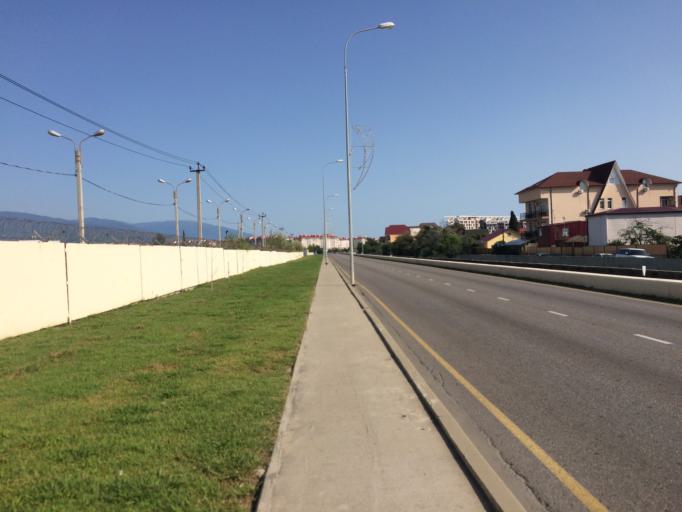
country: RU
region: Krasnodarskiy
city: Adler
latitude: 43.3950
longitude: 39.9833
